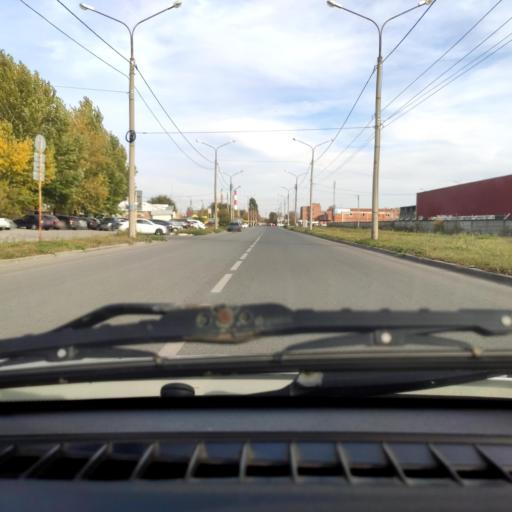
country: RU
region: Samara
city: Tol'yatti
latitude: 53.5419
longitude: 49.4194
